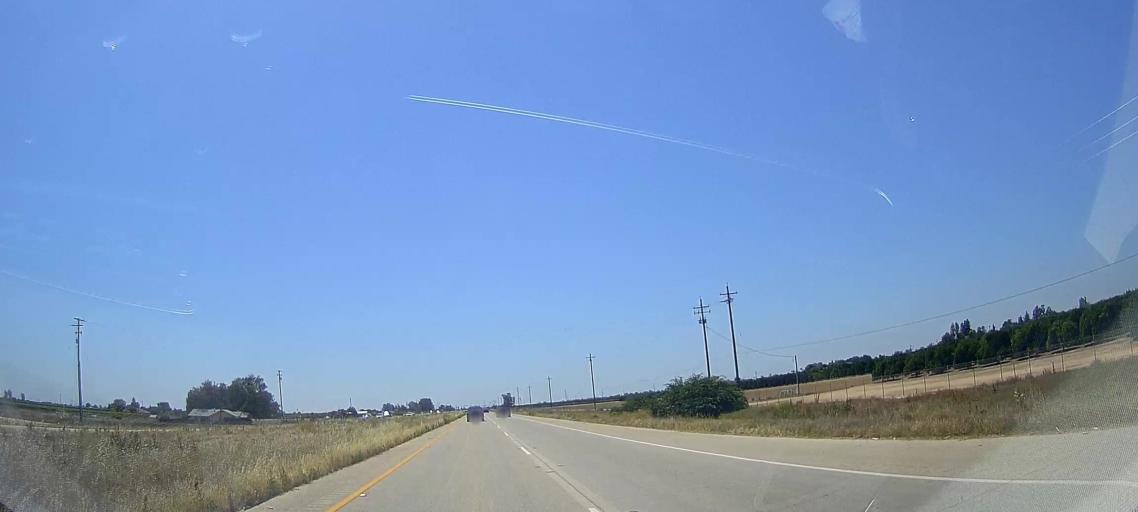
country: US
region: California
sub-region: Fresno County
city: Sanger
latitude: 36.7362
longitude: -119.5648
